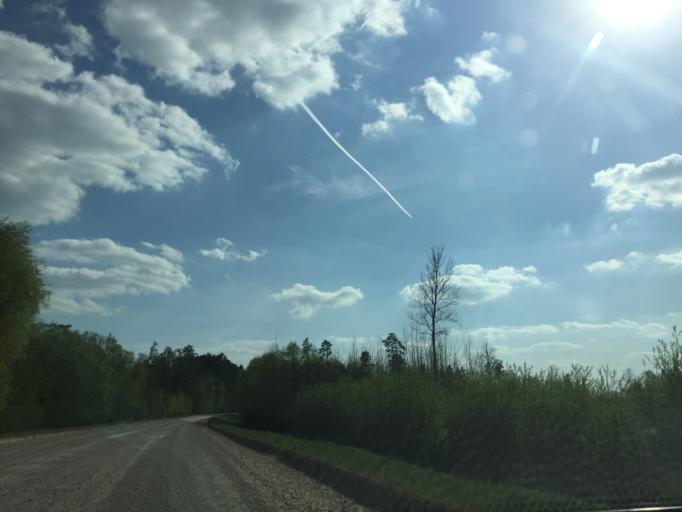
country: LV
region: Vecumnieki
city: Vecumnieki
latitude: 56.5144
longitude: 24.4089
